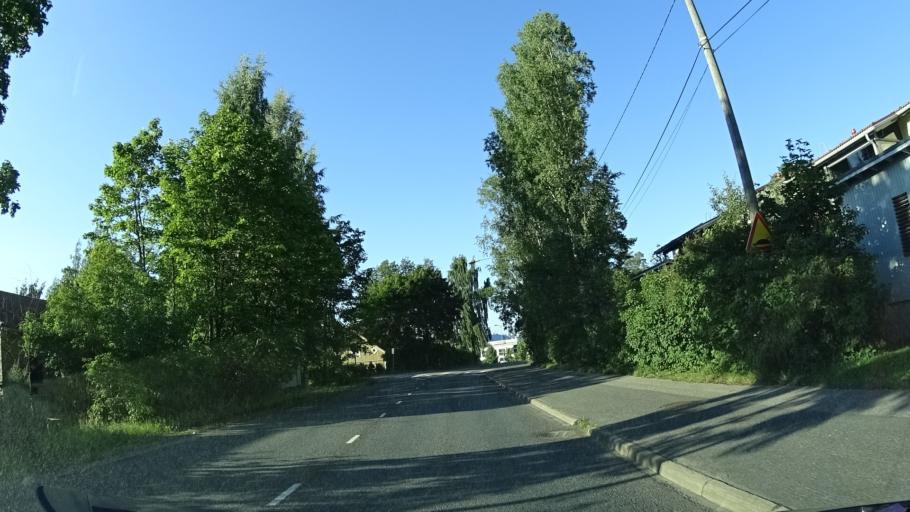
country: FI
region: Uusimaa
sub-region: Helsinki
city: Teekkarikylae
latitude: 60.2586
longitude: 24.8730
